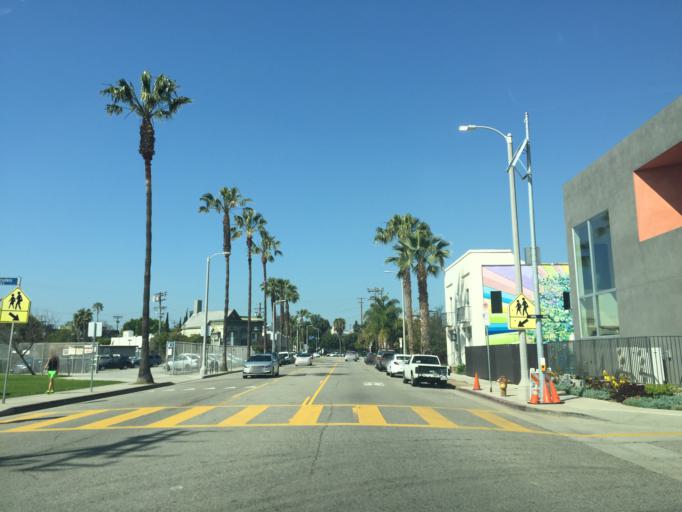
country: US
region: California
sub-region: Los Angeles County
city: Marina del Rey
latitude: 33.9921
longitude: -118.4718
